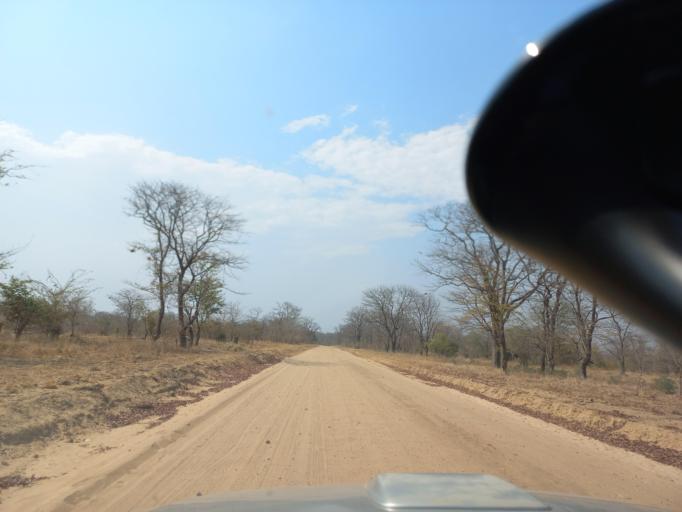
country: ZW
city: Chirundu
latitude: -15.9355
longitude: 28.9148
